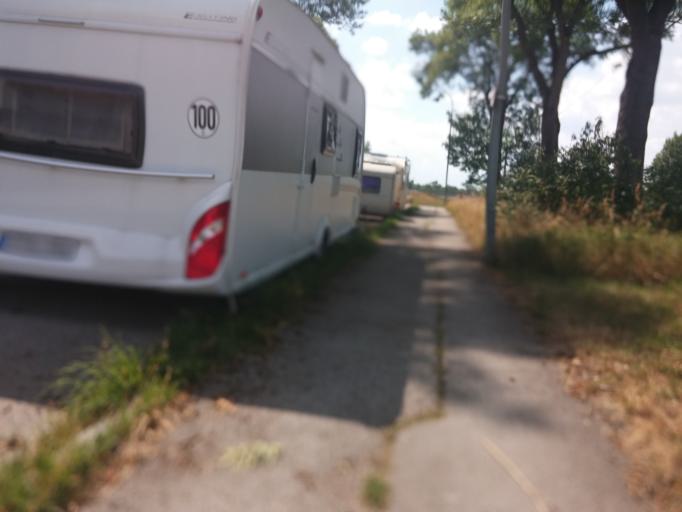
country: DE
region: Bavaria
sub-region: Upper Bavaria
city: Unterhaching
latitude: 48.0821
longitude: 11.6239
